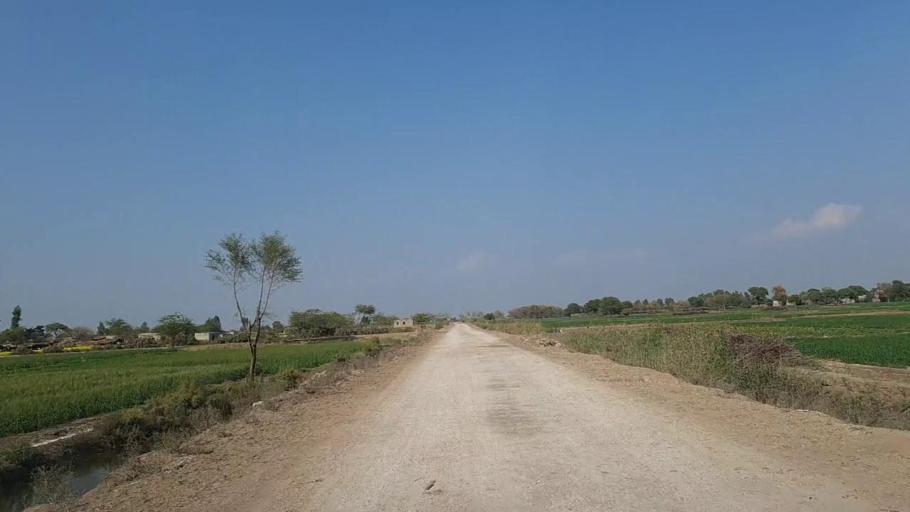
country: PK
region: Sindh
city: Jam Sahib
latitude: 26.2944
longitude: 68.5832
